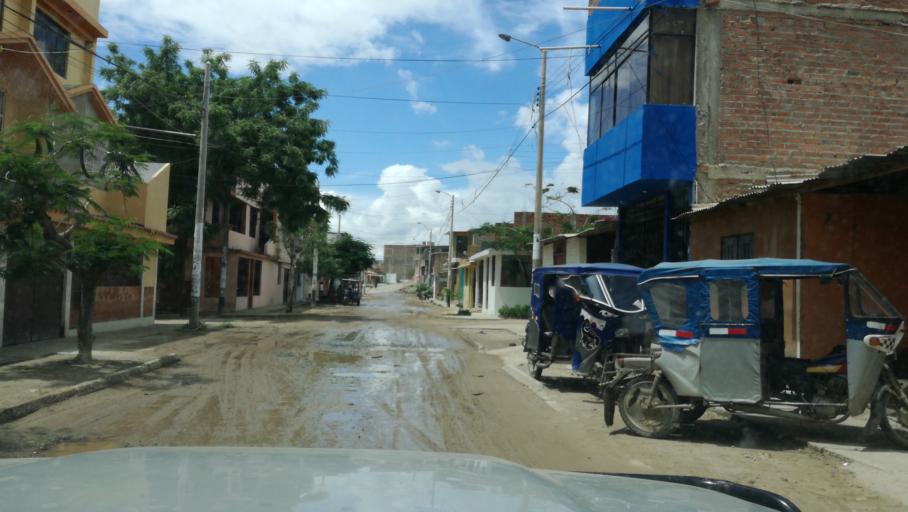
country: PE
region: Piura
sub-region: Provincia de Piura
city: Piura
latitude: -5.1766
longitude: -80.6458
